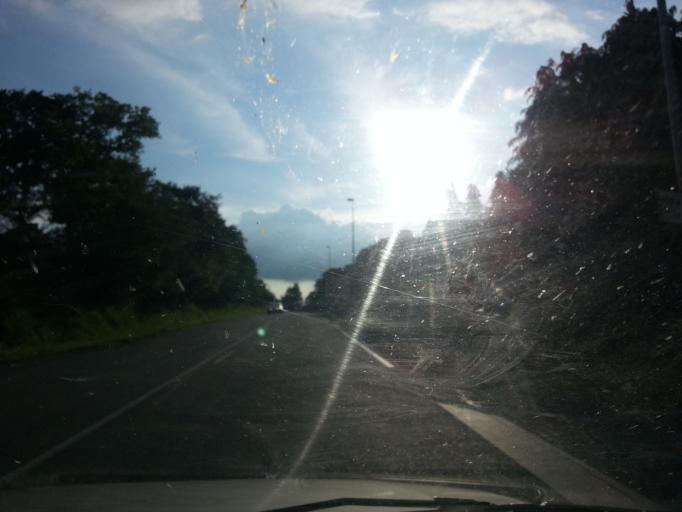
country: FR
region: Brittany
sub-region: Departement du Finistere
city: Carhaix-Plouguer
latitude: 48.2711
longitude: -3.5814
